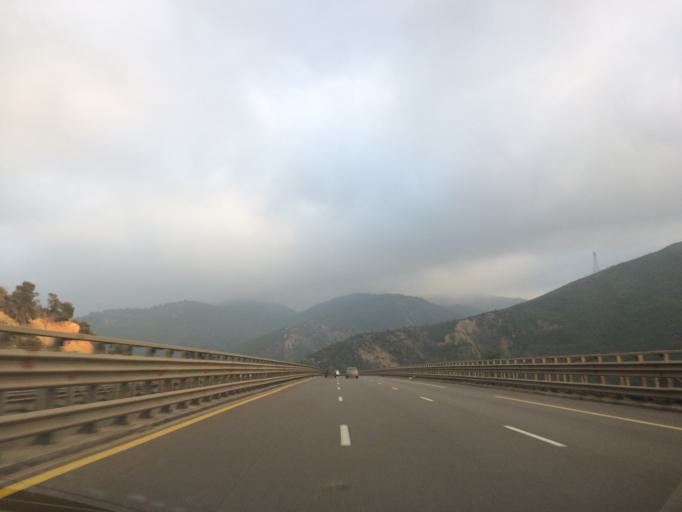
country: DZ
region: Tipaza
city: El Affroun
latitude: 36.4025
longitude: 2.5488
